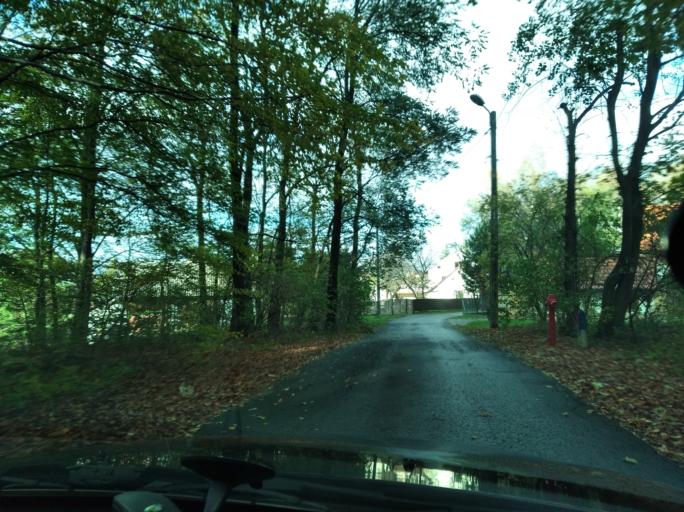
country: PL
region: Subcarpathian Voivodeship
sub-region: Powiat debicki
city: Debica
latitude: 50.0336
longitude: 21.4532
